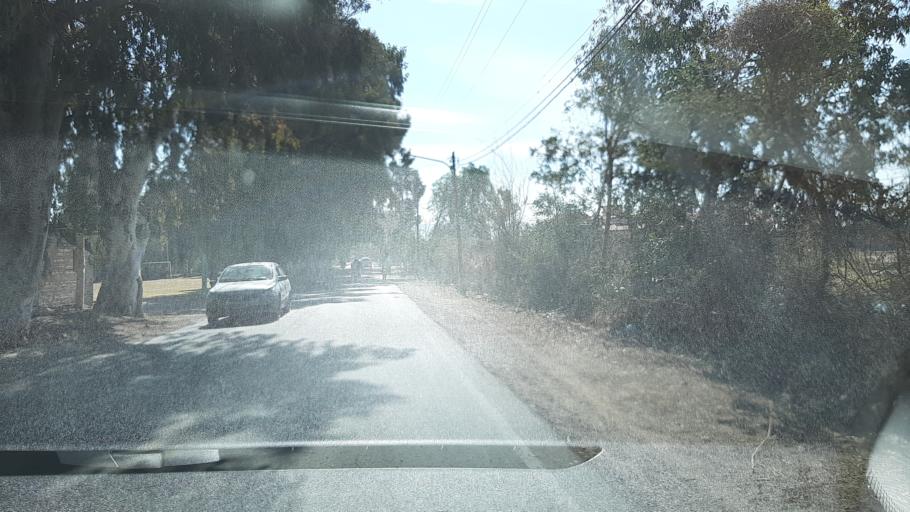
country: AR
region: San Juan
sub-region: Departamento de Rivadavia
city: Rivadavia
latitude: -31.5349
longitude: -68.6177
